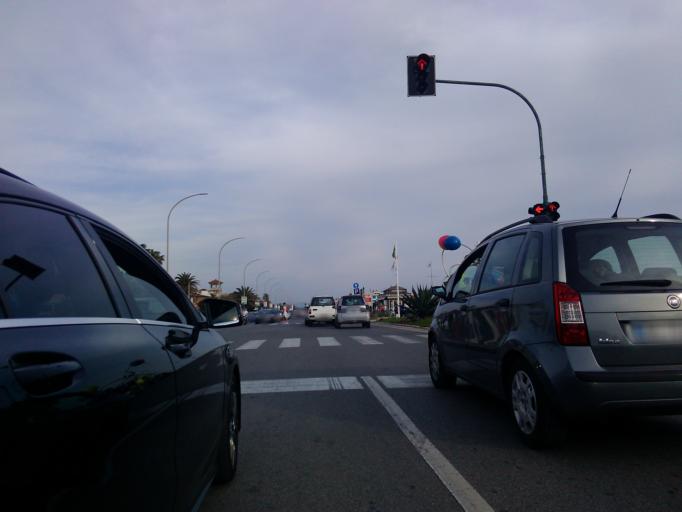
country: IT
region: Tuscany
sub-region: Provincia di Massa-Carrara
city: Massa
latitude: 44.0080
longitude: 10.0987
